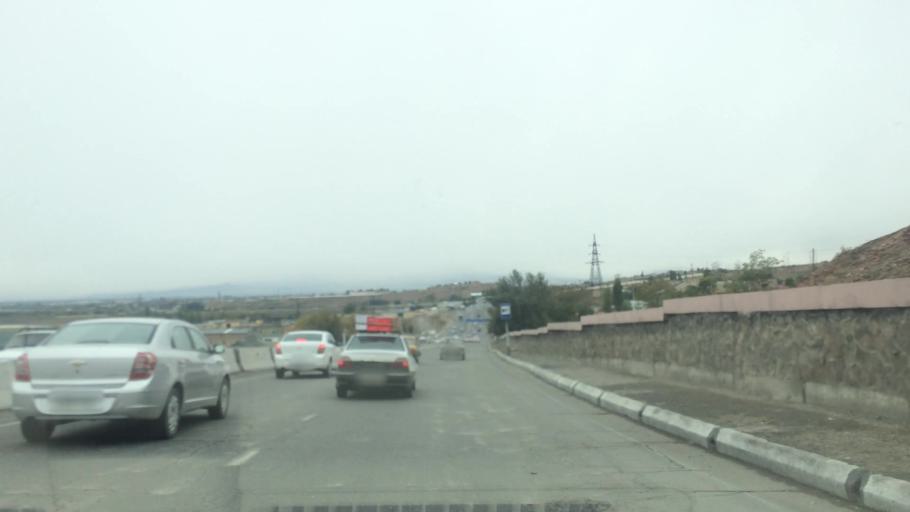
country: UZ
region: Samarqand
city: Jomboy
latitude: 39.6836
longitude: 67.0513
